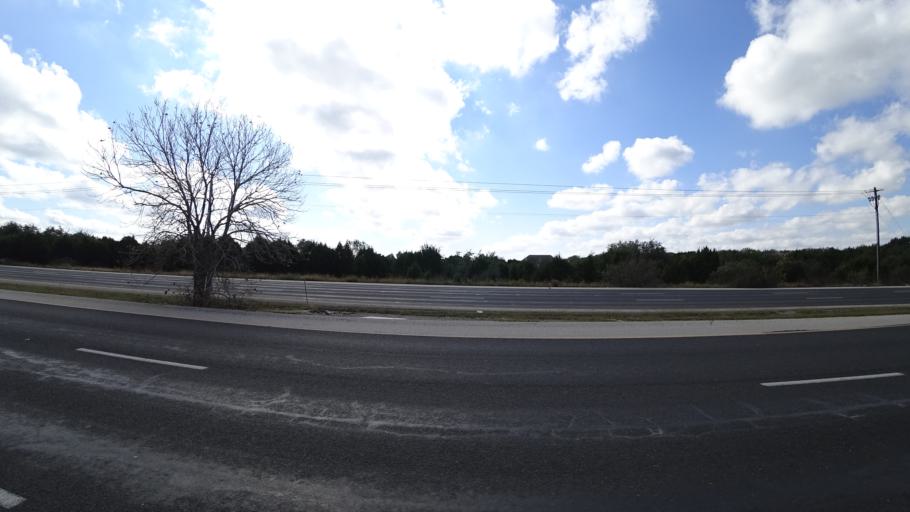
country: US
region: Texas
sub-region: Travis County
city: Barton Creek
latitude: 30.2571
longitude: -97.8809
